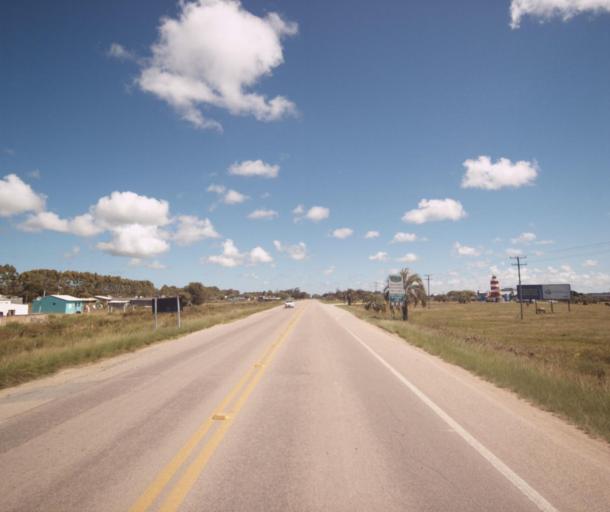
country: BR
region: Rio Grande do Sul
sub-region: Santa Vitoria Do Palmar
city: Santa Vitoria do Palmar
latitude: -33.5296
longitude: -53.3443
